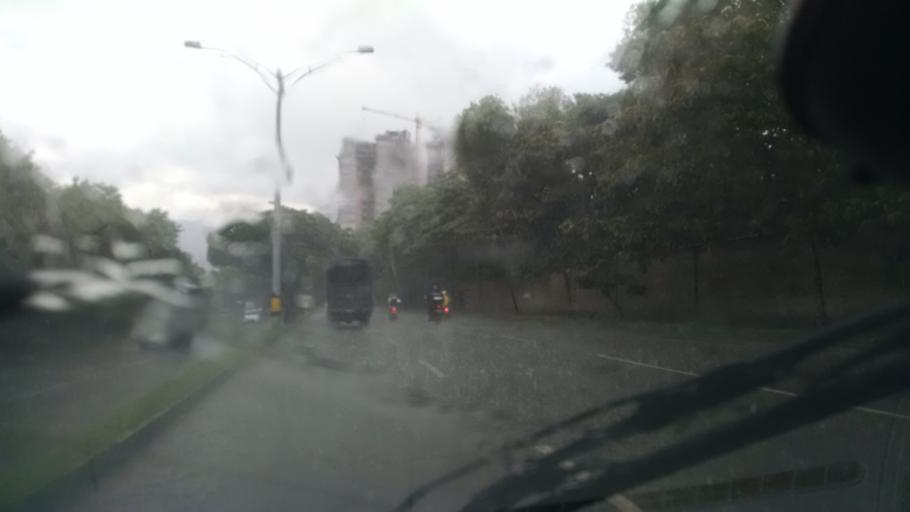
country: CO
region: Antioquia
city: Medellin
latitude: 6.2598
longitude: -75.5826
